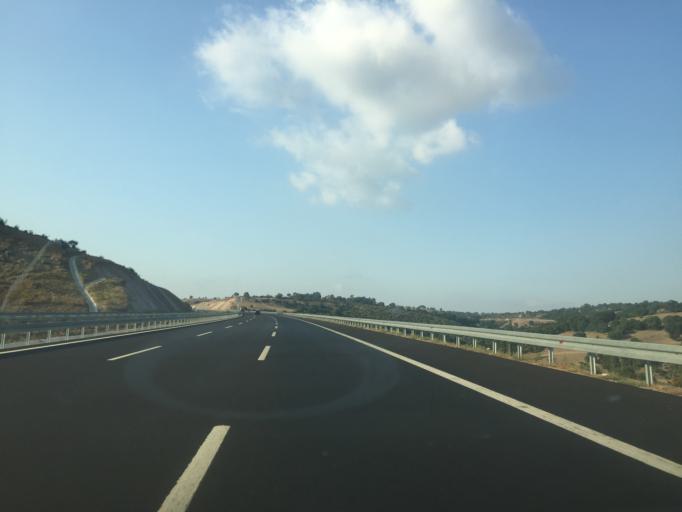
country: TR
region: Balikesir
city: Ertugrul
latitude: 39.5972
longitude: 27.7029
